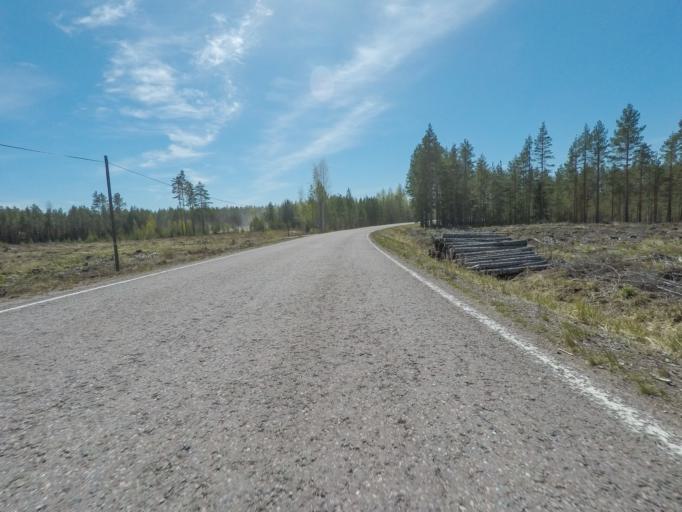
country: FI
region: Uusimaa
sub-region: Helsinki
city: Kaerkoelae
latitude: 60.6013
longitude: 23.8122
